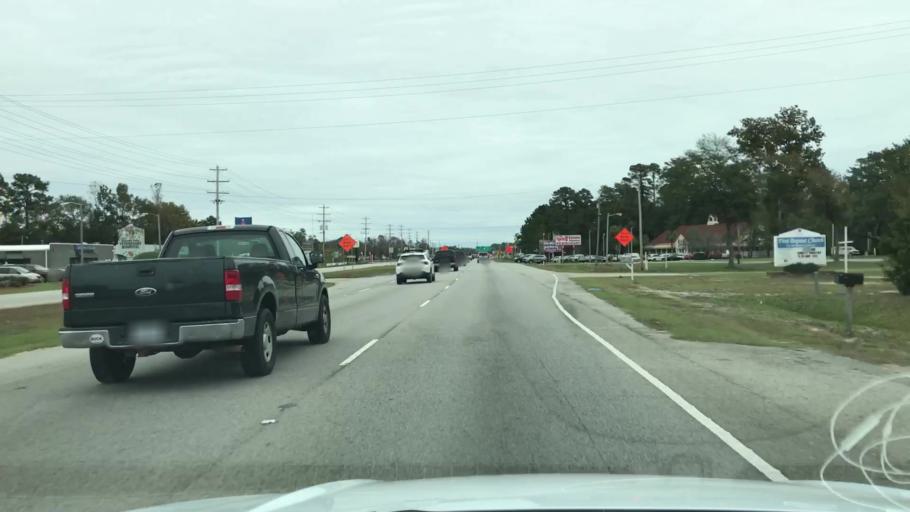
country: US
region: South Carolina
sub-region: Georgetown County
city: Murrells Inlet
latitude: 33.5632
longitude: -79.0380
